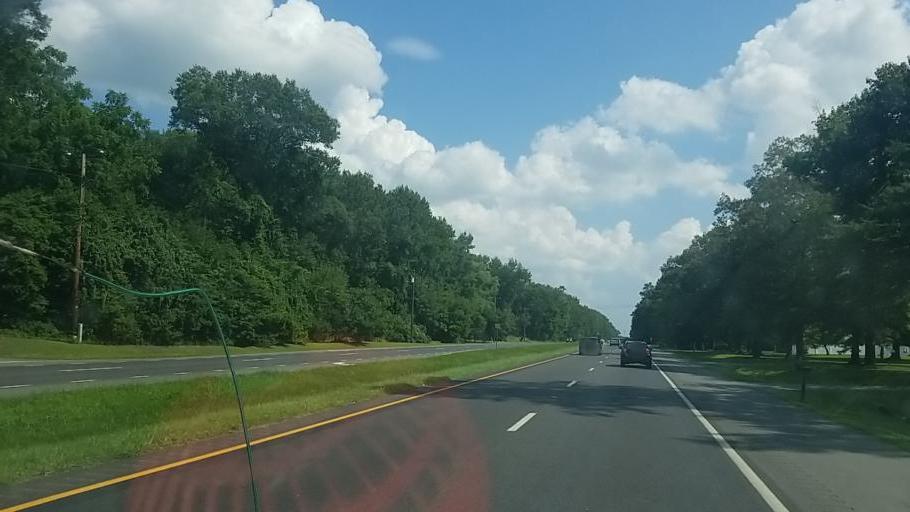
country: US
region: Delaware
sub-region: Sussex County
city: Millsboro
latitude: 38.5608
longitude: -75.2738
